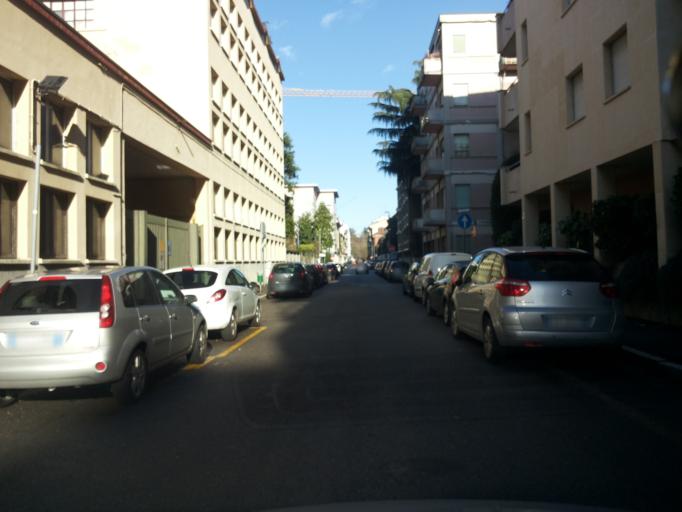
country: IT
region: Piedmont
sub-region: Provincia di Novara
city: Novara
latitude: 45.4411
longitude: 8.6116
